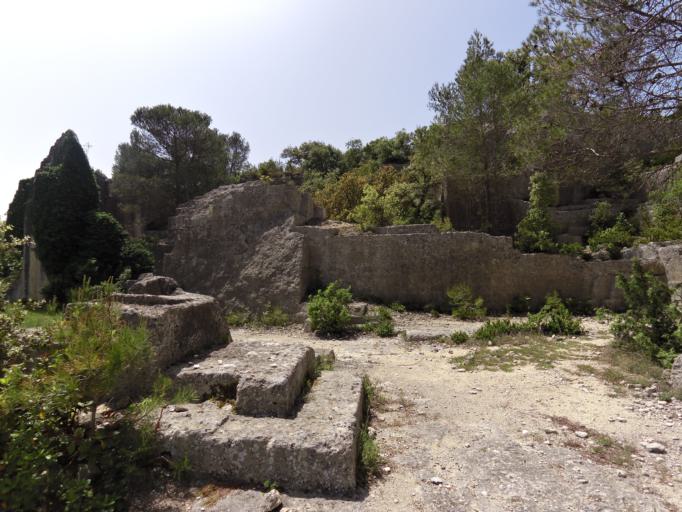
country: FR
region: Languedoc-Roussillon
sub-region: Departement du Gard
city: Villevieille
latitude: 43.7739
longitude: 4.1193
